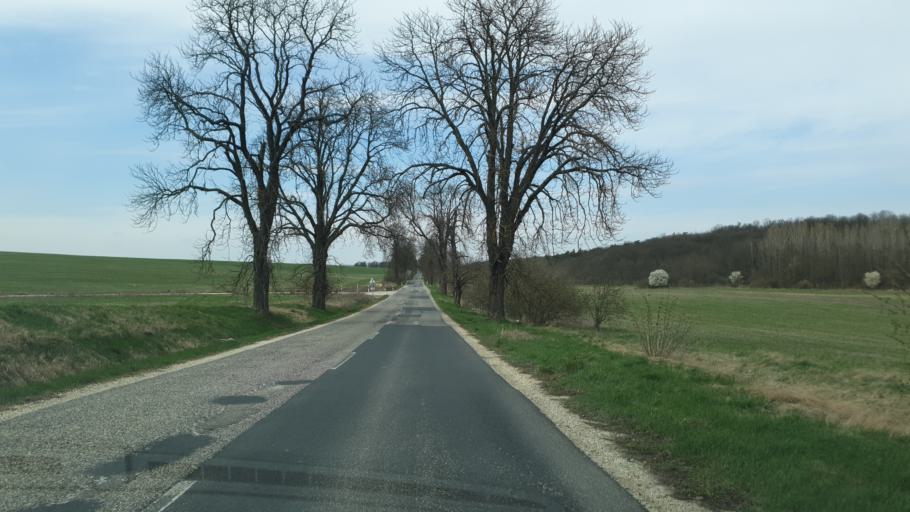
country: HU
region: Fejer
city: Etyek
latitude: 47.4642
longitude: 18.7242
